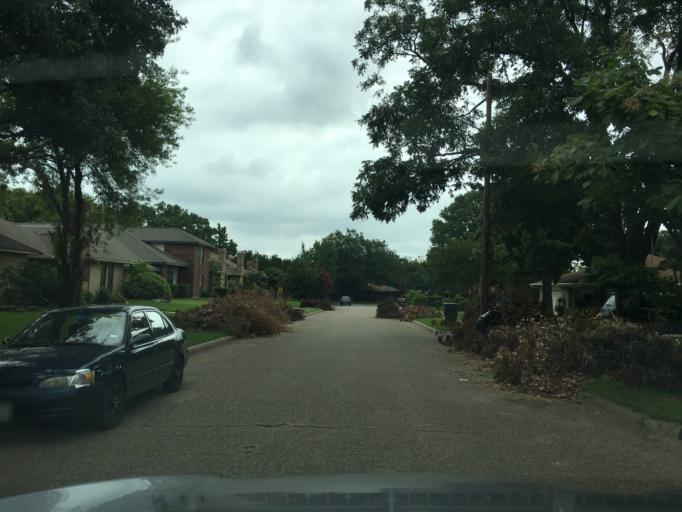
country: US
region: Texas
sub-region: Dallas County
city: Highland Park
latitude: 32.8534
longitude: -96.7456
